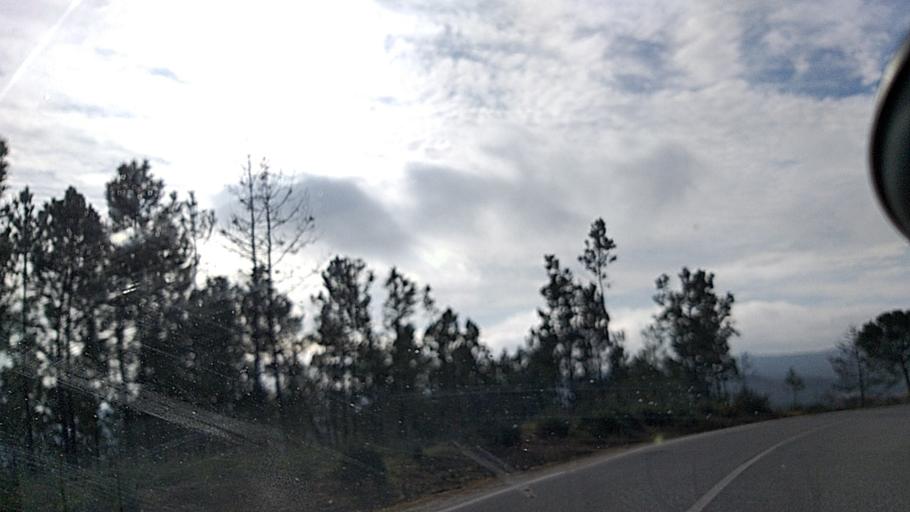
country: PT
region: Guarda
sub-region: Aguiar da Beira
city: Aguiar da Beira
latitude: 40.7413
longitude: -7.5546
